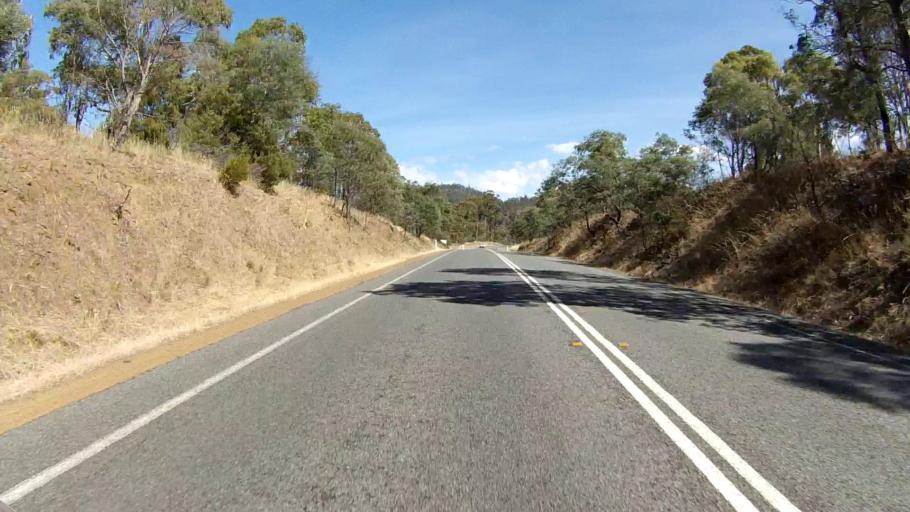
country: AU
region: Tasmania
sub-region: Sorell
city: Sorell
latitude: -42.6068
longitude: 147.6718
